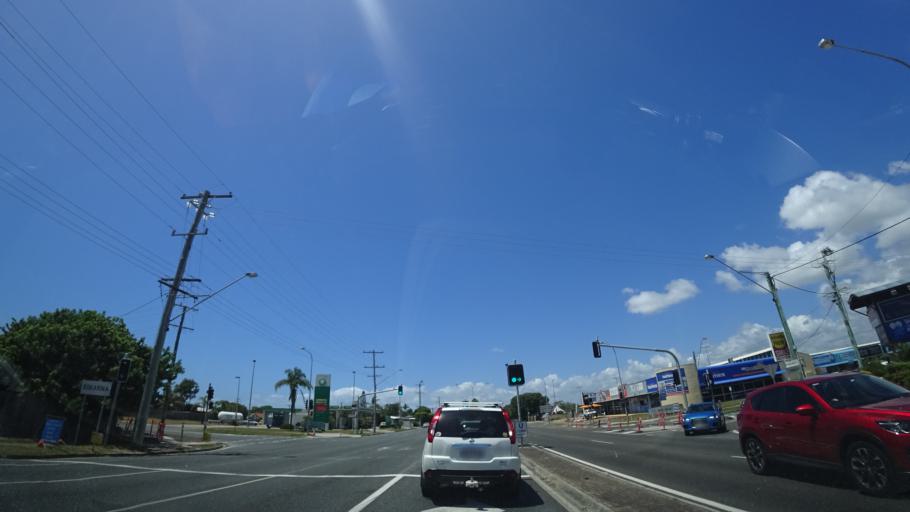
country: AU
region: Queensland
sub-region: Sunshine Coast
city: Mooloolaba
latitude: -26.7306
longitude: 153.1292
